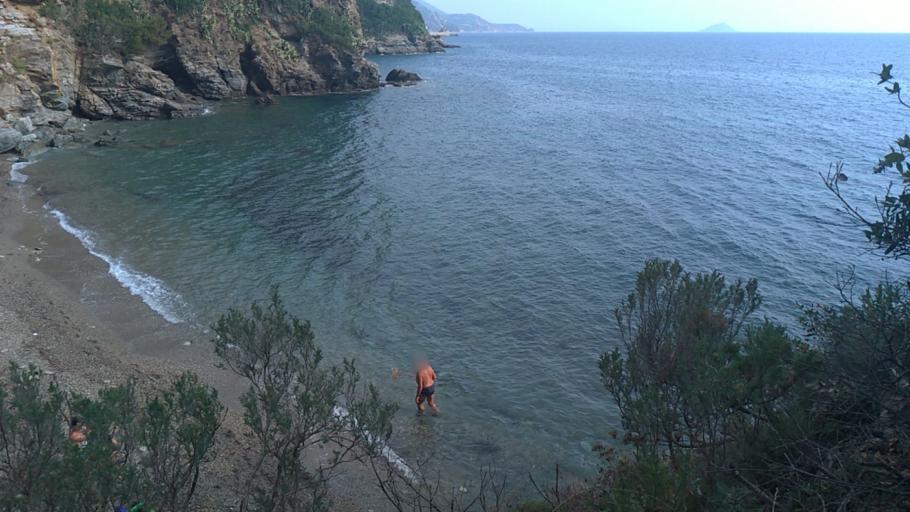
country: IT
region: Tuscany
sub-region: Provincia di Livorno
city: Rio Marina
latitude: 42.8057
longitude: 10.4297
